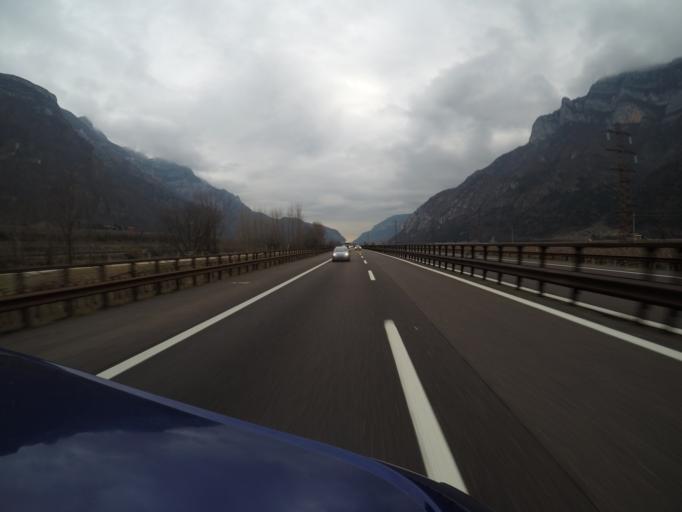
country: IT
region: Trentino-Alto Adige
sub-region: Provincia di Trento
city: Avio
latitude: 45.7275
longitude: 10.9422
